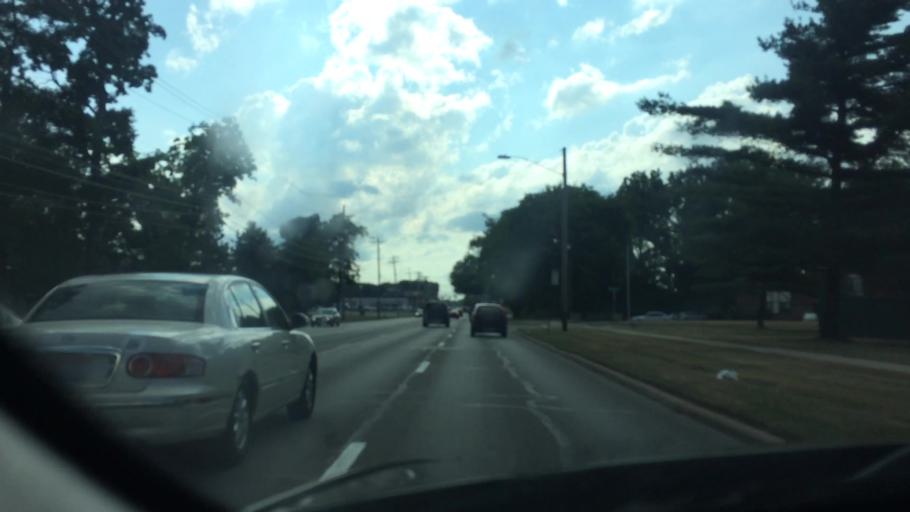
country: US
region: Ohio
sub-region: Lucas County
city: Maumee
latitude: 41.5947
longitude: -83.6601
